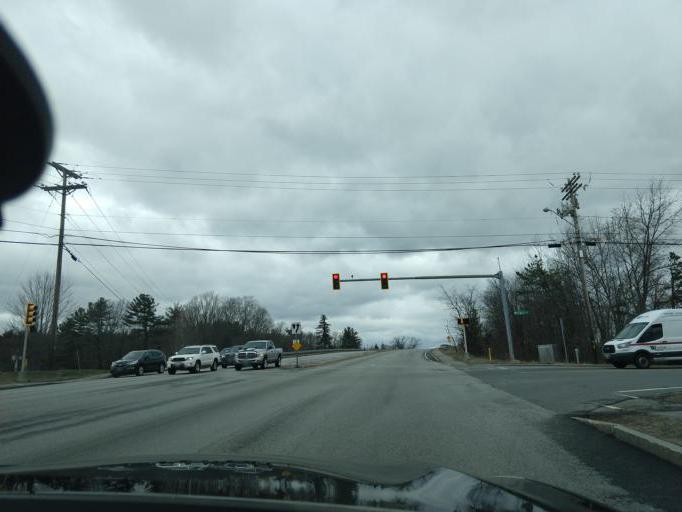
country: US
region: New Hampshire
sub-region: Rockingham County
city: Plaistow
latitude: 42.8272
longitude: -71.1067
